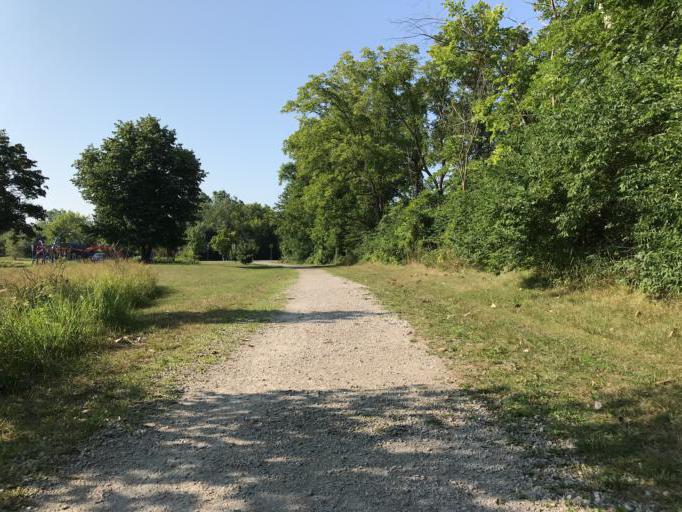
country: US
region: Michigan
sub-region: Washtenaw County
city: Ann Arbor
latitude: 42.2408
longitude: -83.7128
